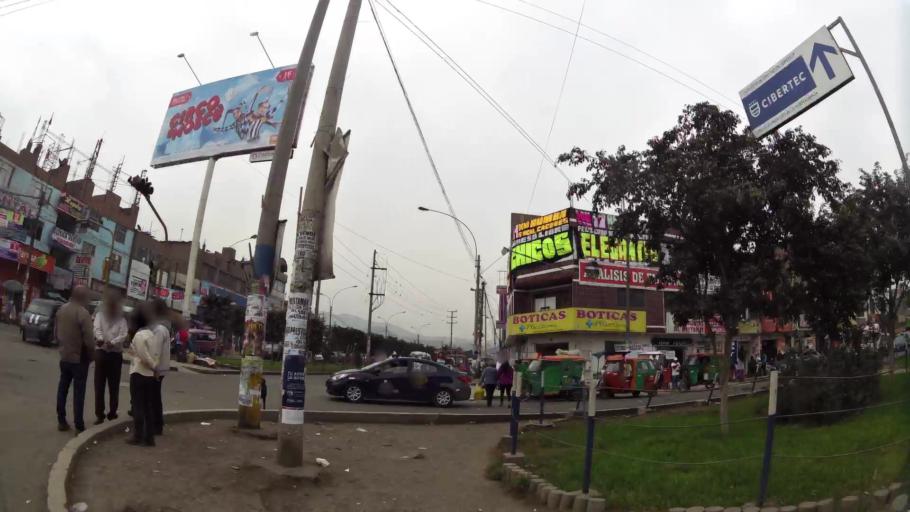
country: PE
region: Lima
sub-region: Lima
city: Independencia
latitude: -11.9683
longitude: -77.0041
